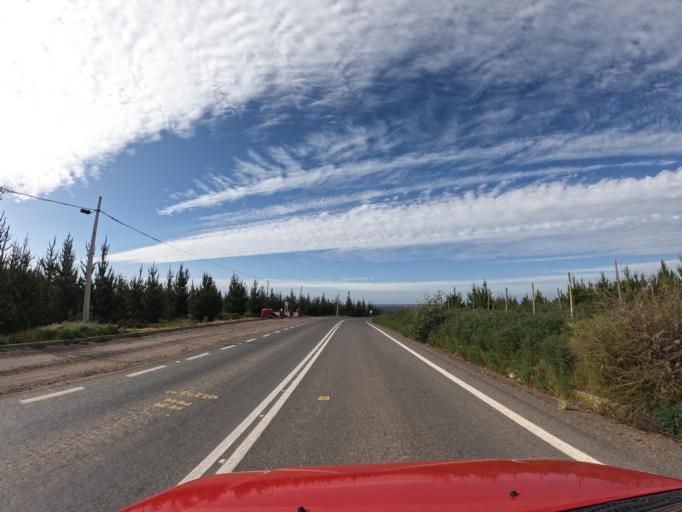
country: CL
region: O'Higgins
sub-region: Provincia de Colchagua
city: Santa Cruz
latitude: -34.3043
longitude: -71.8336
